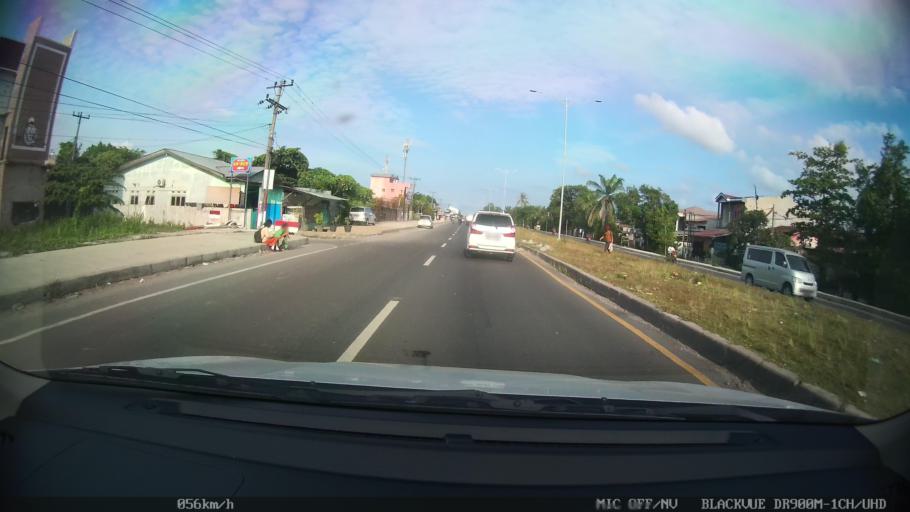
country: ID
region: North Sumatra
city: Sunggal
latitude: 3.6159
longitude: 98.6321
